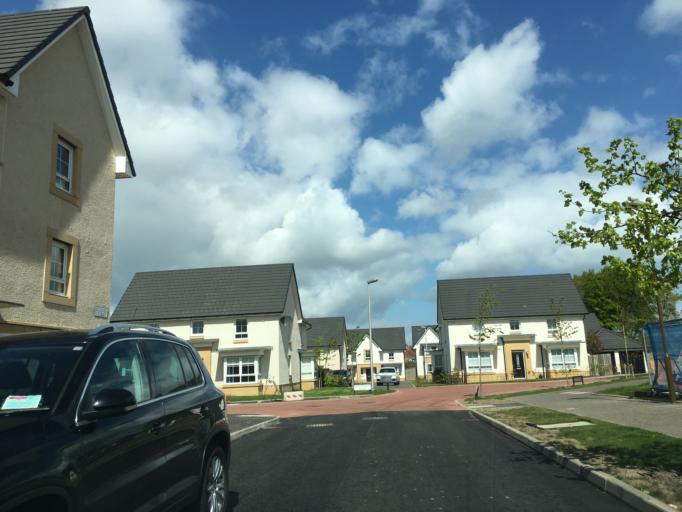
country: GB
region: Scotland
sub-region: Edinburgh
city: Edinburgh
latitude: 55.9048
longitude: -3.2032
